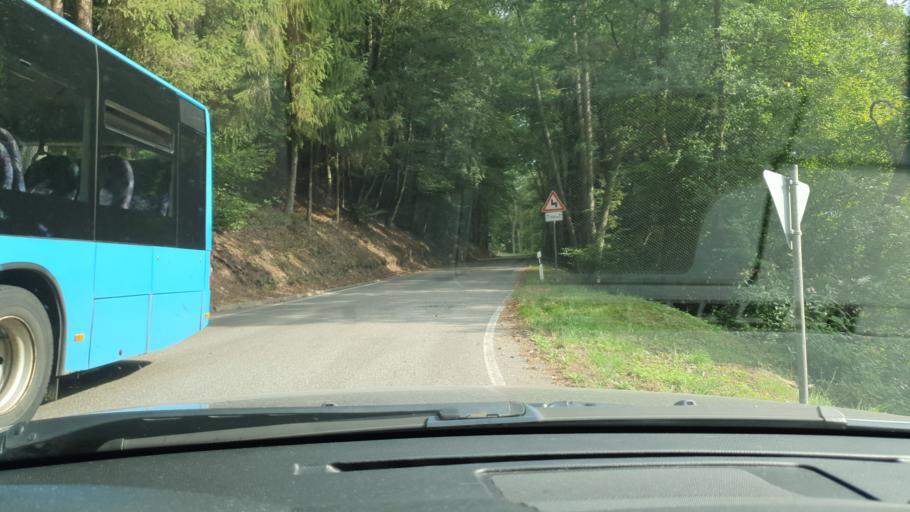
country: DE
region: Rheinland-Pfalz
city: Gerhardsbrunn
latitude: 49.3373
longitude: 7.5205
